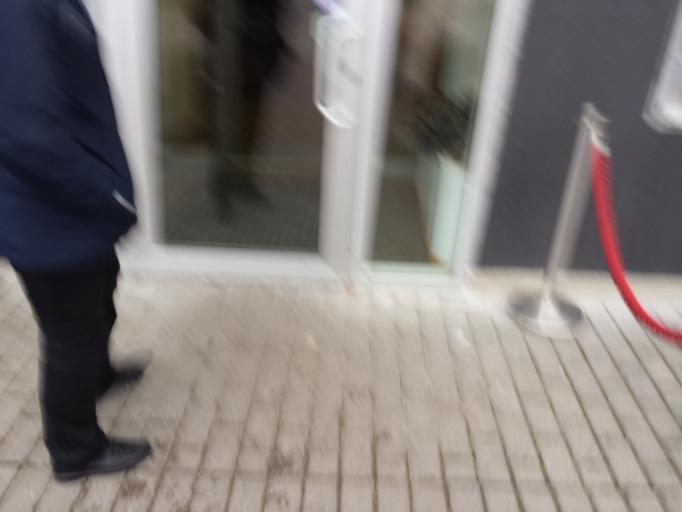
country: SE
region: Stockholm
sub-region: Sundbybergs Kommun
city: Sundbyberg
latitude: 59.3535
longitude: 17.9755
